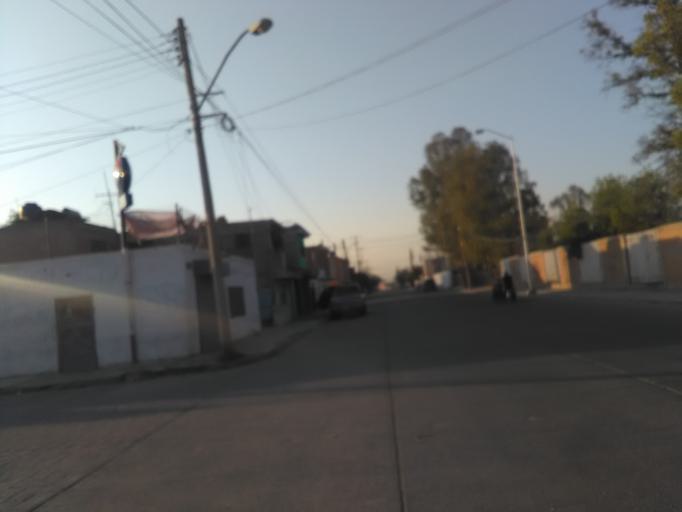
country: MX
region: Durango
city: Victoria de Durango
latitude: 24.0492
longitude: -104.6458
